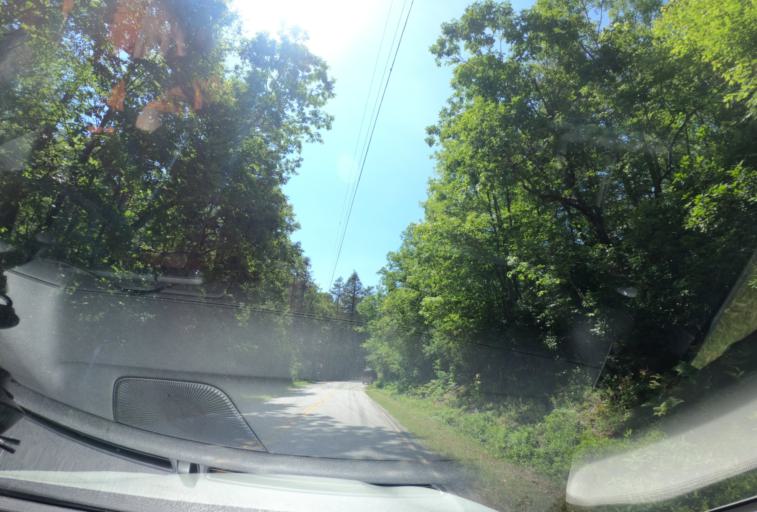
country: US
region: North Carolina
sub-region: Transylvania County
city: Brevard
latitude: 35.1839
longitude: -82.6446
